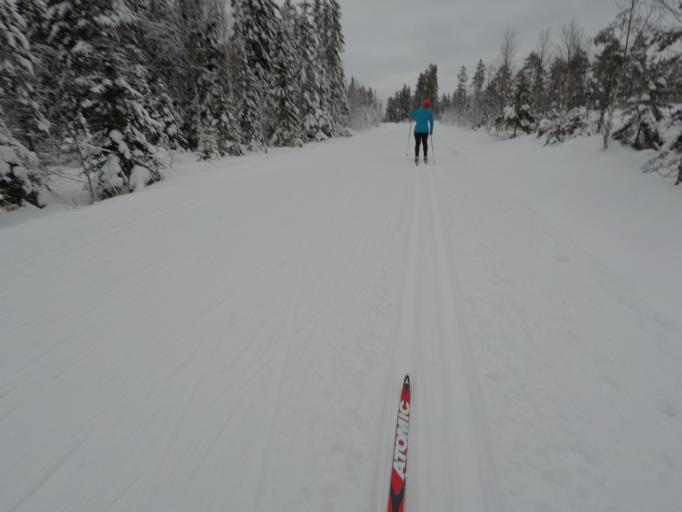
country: SE
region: Dalarna
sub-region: Ludvika Kommun
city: Abborrberget
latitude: 60.1445
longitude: 14.4867
